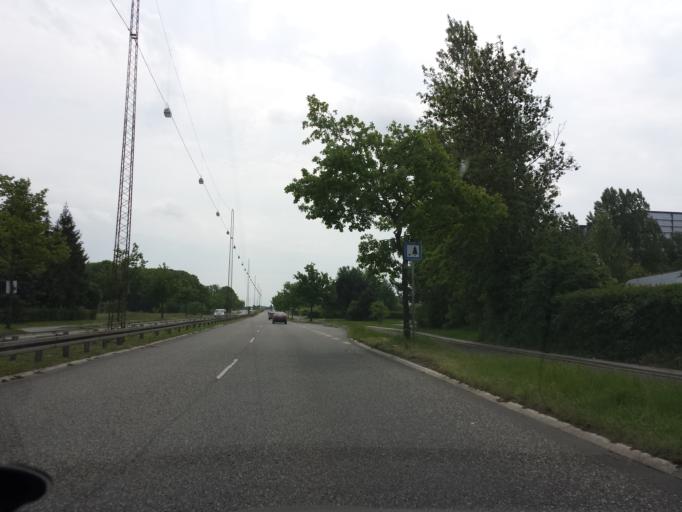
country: DK
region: Capital Region
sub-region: Herlev Kommune
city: Herlev
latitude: 55.7097
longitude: 12.4203
